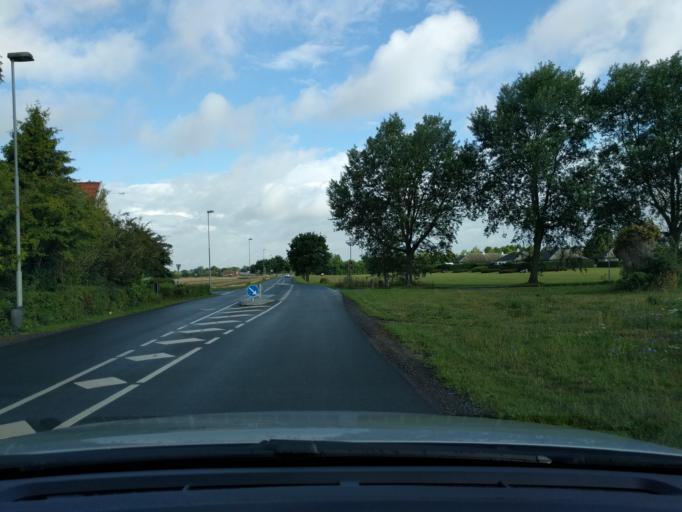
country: DK
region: South Denmark
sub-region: Odense Kommune
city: Seden
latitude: 55.4180
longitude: 10.4475
